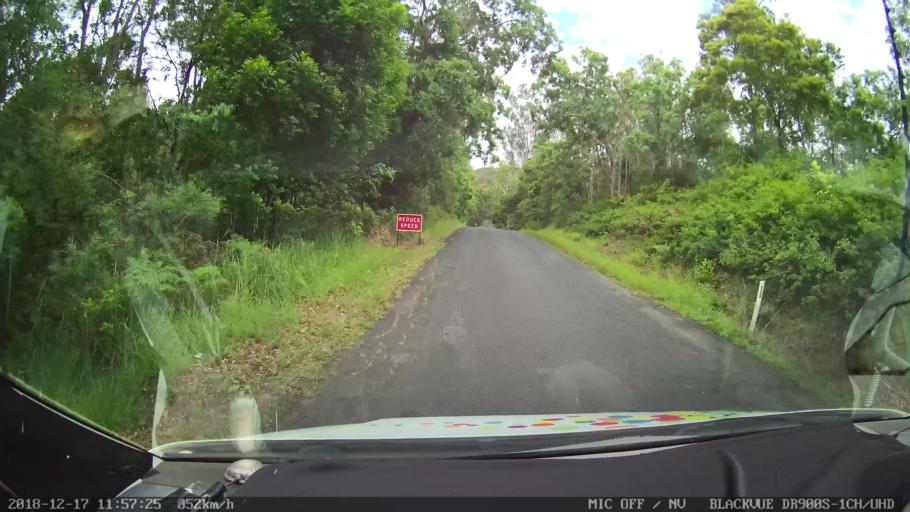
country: AU
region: New South Wales
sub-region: Kyogle
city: Kyogle
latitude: -28.5407
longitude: 152.5738
